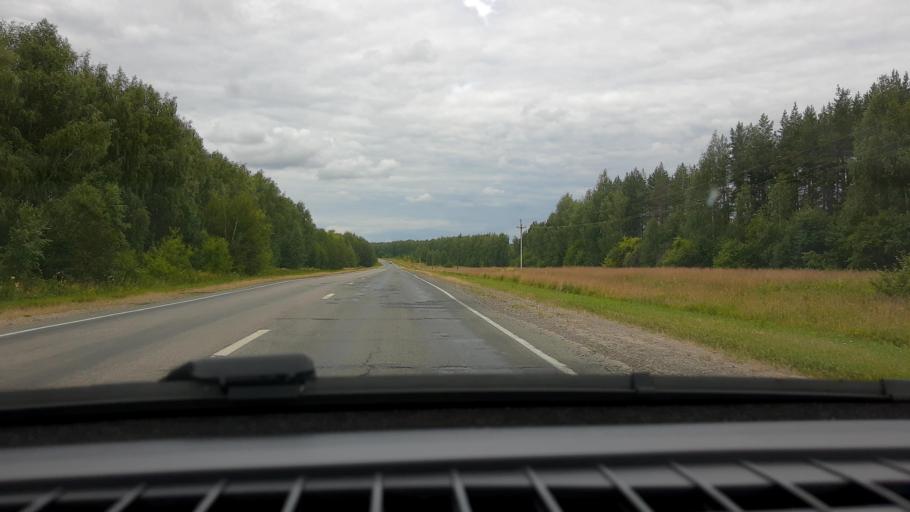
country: RU
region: Nizjnij Novgorod
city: Knyaginino
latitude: 55.7161
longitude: 45.2031
